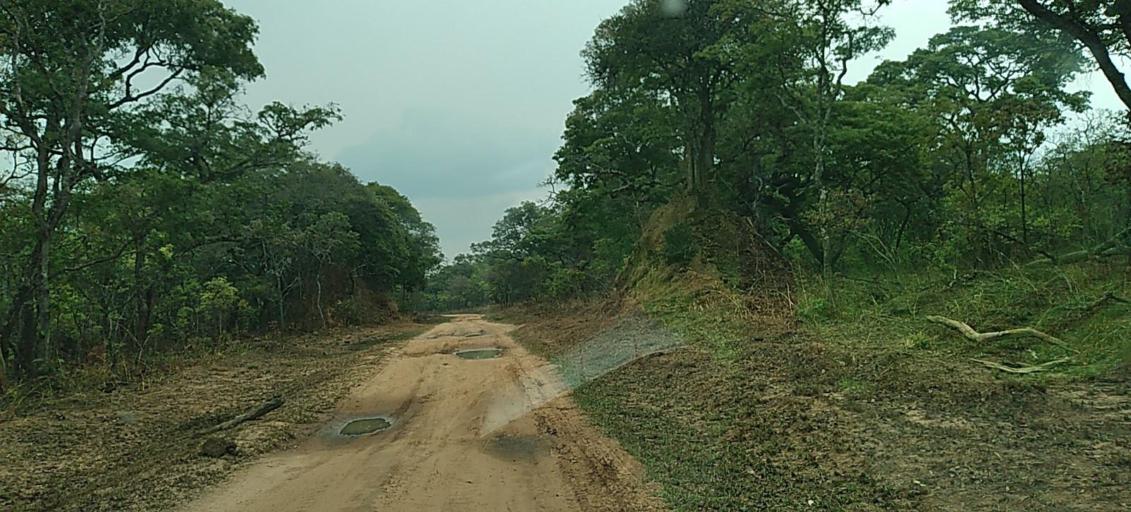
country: ZM
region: North-Western
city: Mwinilunga
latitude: -11.4665
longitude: 24.4722
